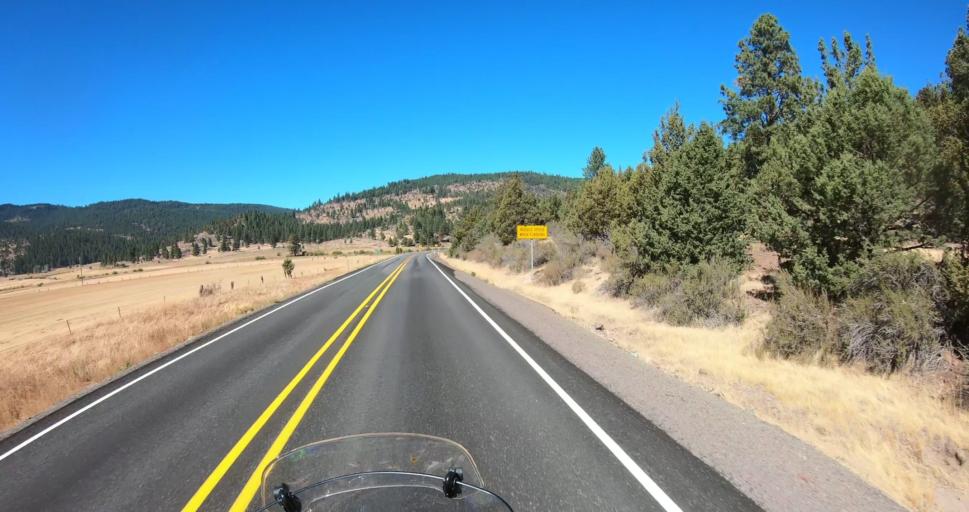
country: US
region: Oregon
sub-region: Lake County
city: Lakeview
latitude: 42.3818
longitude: -120.3045
